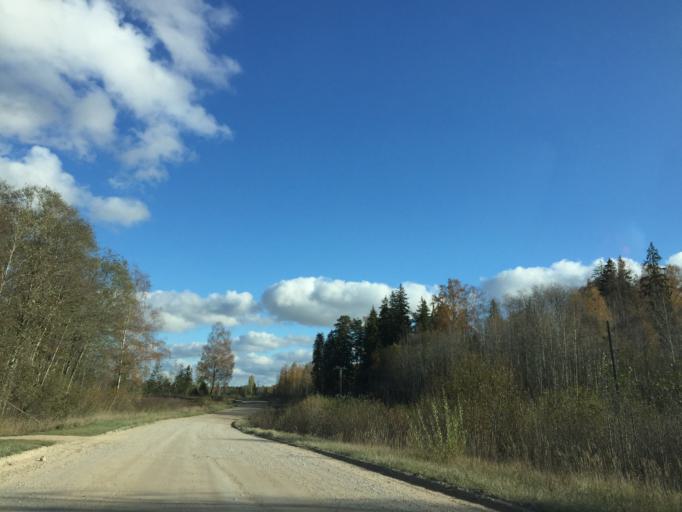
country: LV
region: Tukuma Rajons
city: Tukums
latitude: 56.9617
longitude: 22.9947
